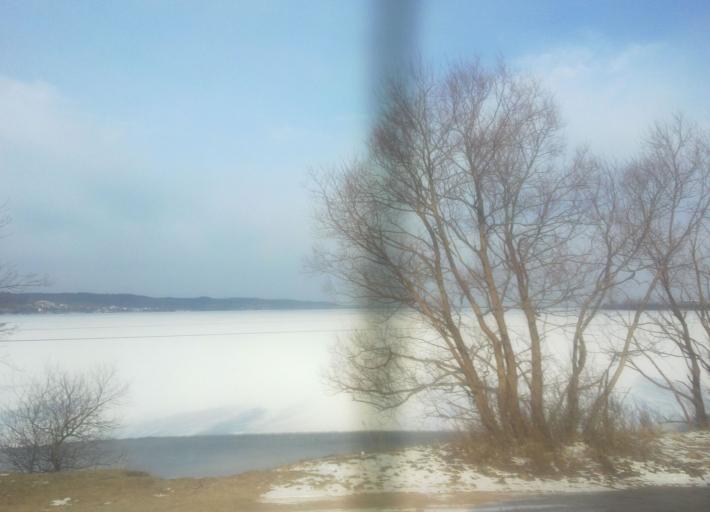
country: PL
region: Pomeranian Voivodeship
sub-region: Powiat wejherowski
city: Gniewino
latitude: 54.7323
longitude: 18.0892
